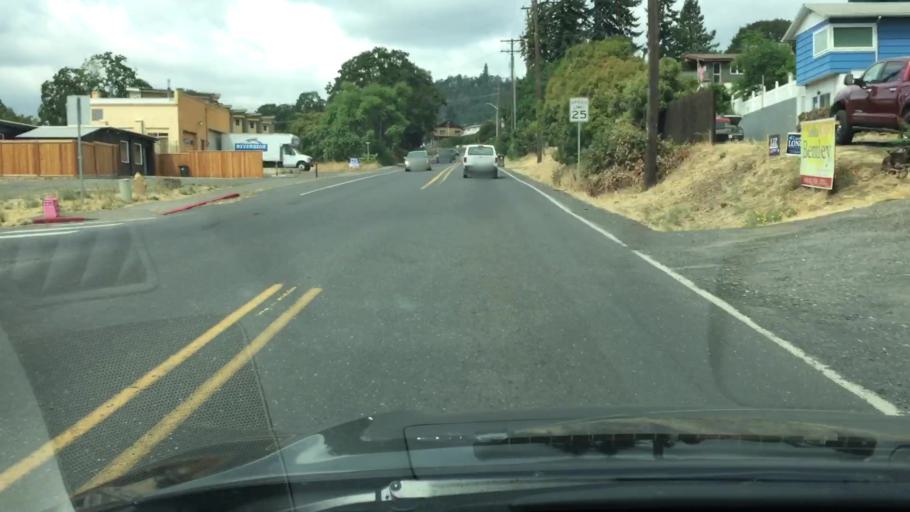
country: US
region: Washington
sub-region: Klickitat County
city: White Salmon
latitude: 45.7254
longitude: -121.4791
